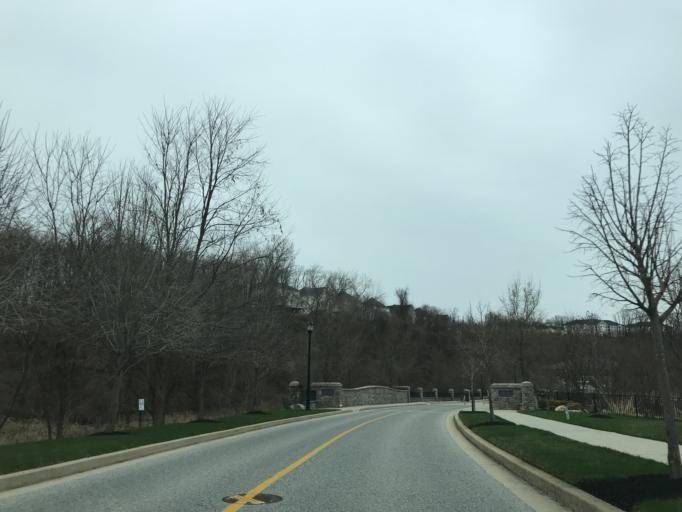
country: US
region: Maryland
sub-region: Baltimore County
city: Pikesville
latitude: 39.3829
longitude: -76.6973
